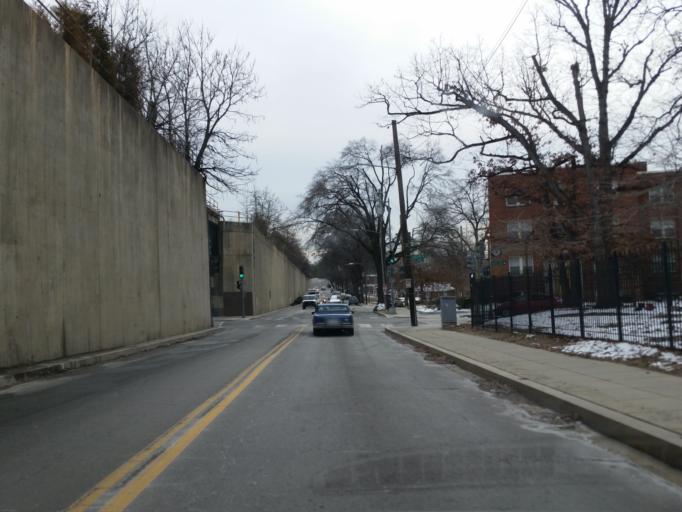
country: US
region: Maryland
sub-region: Montgomery County
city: Takoma Park
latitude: 38.9728
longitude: -77.0166
